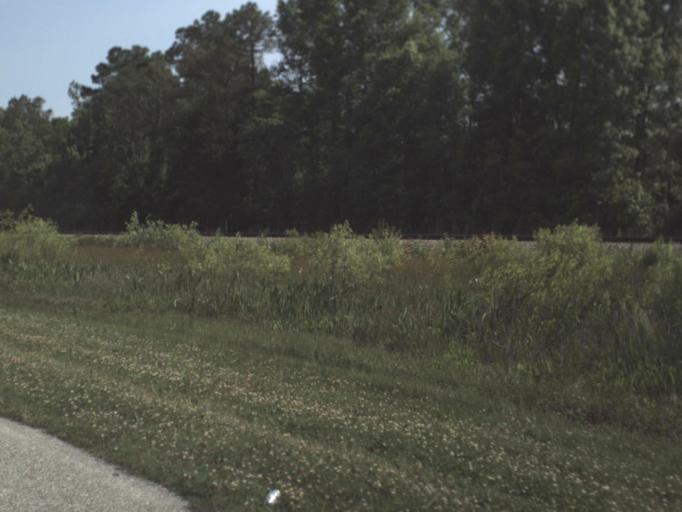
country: US
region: Florida
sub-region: Saint Johns County
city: Villano Beach
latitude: 29.9840
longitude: -81.3666
